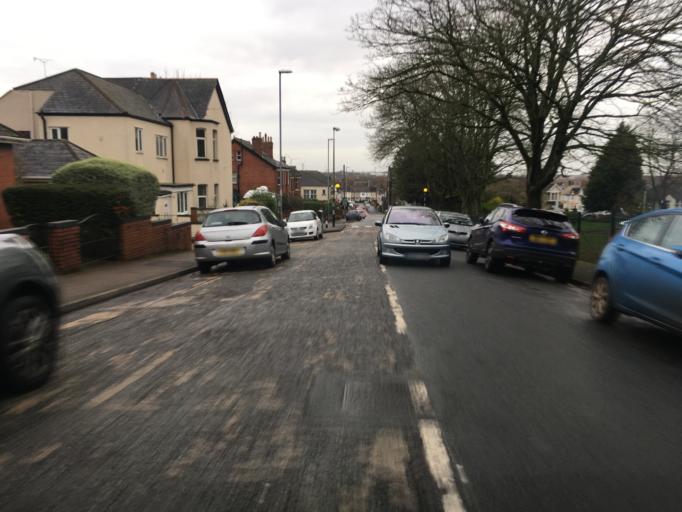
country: GB
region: Wales
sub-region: Newport
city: Caerleon
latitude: 51.5893
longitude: -2.9644
